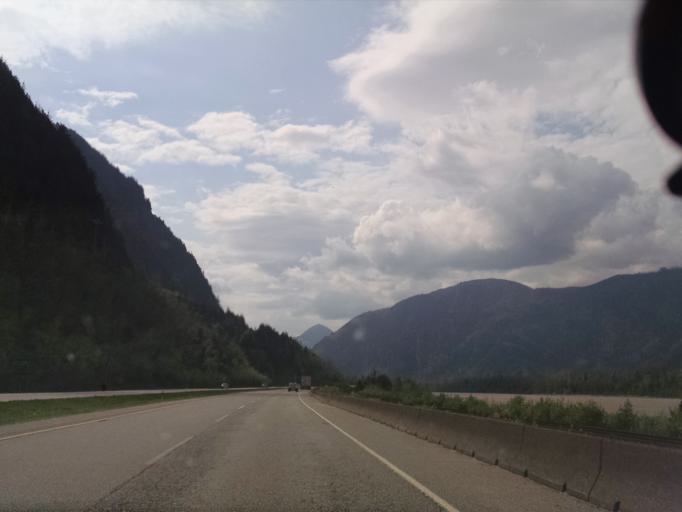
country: CA
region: British Columbia
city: Hope
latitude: 49.3644
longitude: -121.5332
